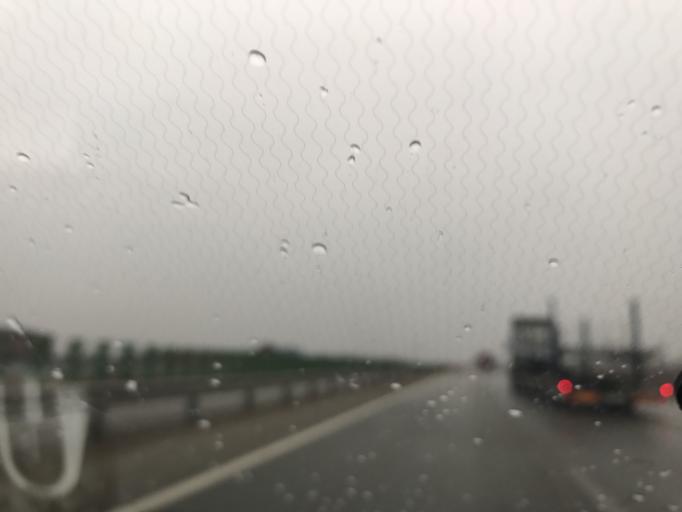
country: RU
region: Krasnodarskiy
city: Krylovskaya
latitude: 46.2933
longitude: 39.8212
